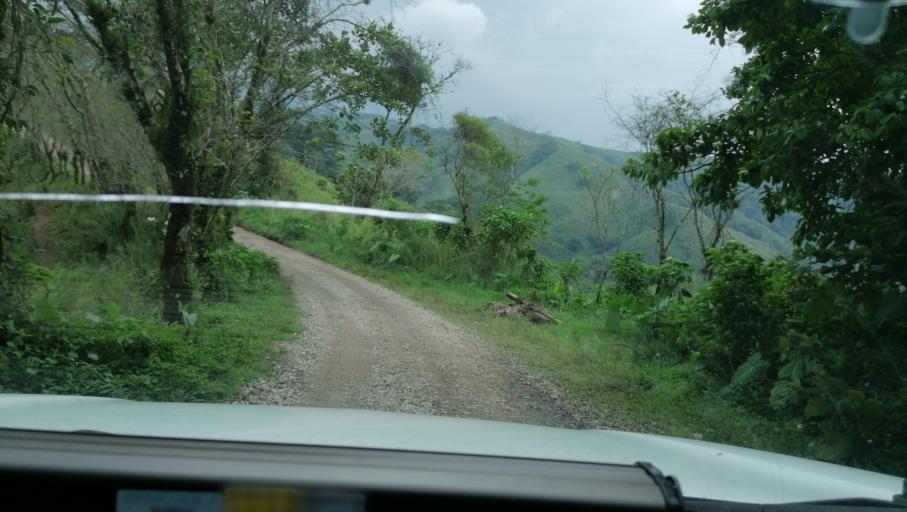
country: MX
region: Chiapas
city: Ixtacomitan
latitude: 17.3493
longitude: -93.1424
